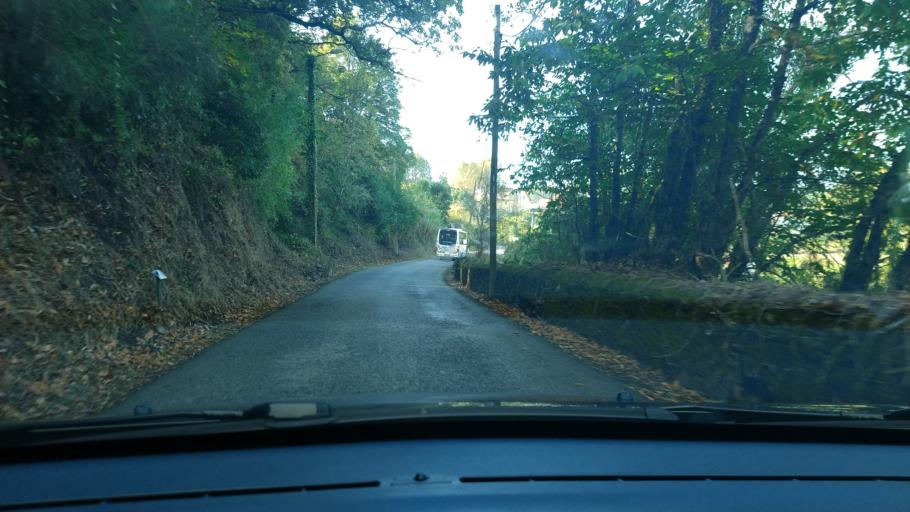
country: PT
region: Lisbon
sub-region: Sintra
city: Colares
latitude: 38.7980
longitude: -9.4420
